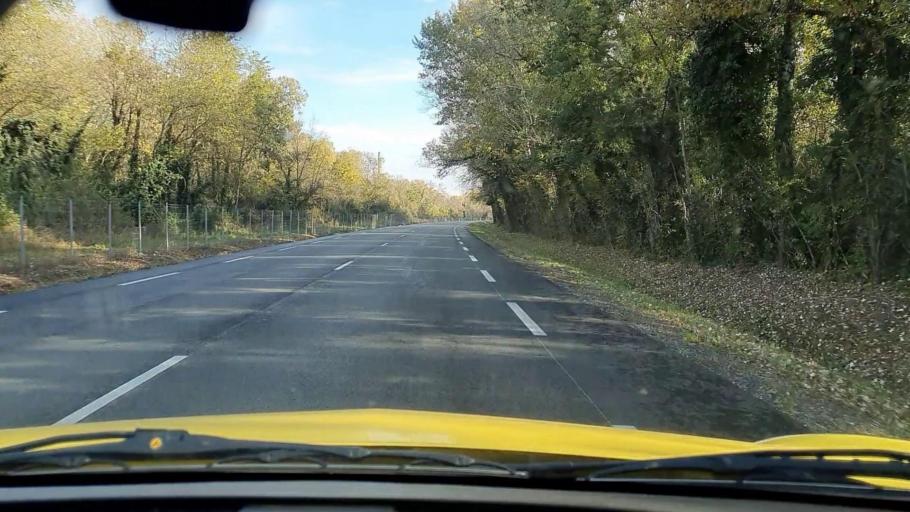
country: FR
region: Languedoc-Roussillon
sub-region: Departement du Gard
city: Vallabregues
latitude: 43.8700
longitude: 4.6275
